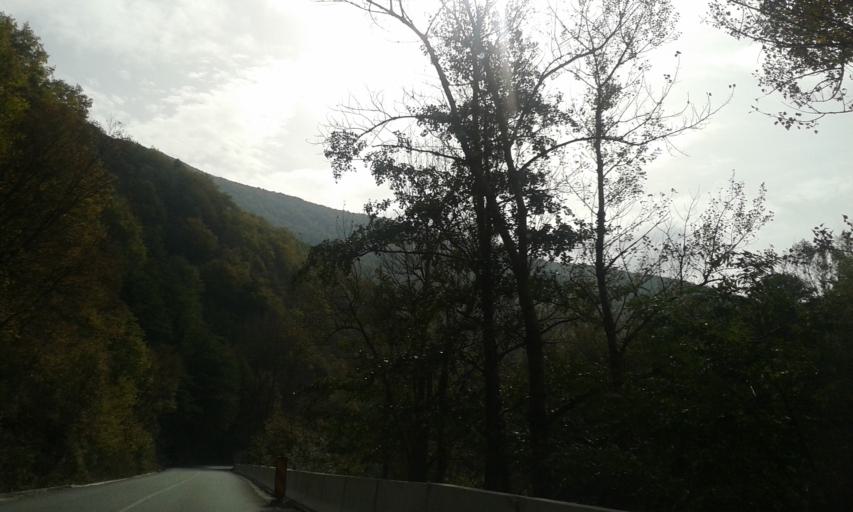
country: RO
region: Gorj
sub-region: Comuna Bumbesti-Jiu
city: Bumbesti-Jiu
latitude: 45.2347
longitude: 23.3899
